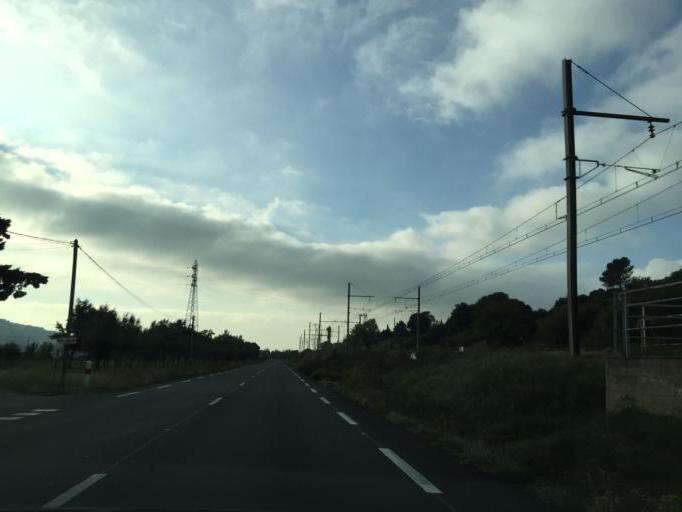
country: FR
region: Rhone-Alpes
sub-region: Departement de l'Ardeche
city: Viviers
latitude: 44.4674
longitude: 4.6878
